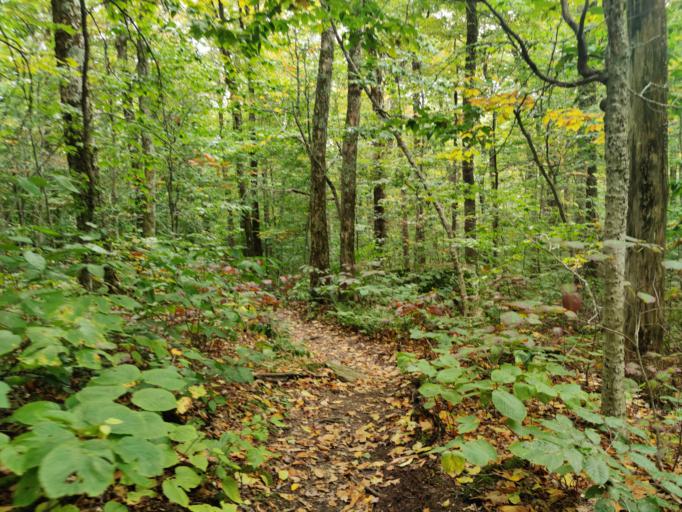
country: US
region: Vermont
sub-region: Bennington County
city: Manchester Center
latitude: 43.2611
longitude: -72.9404
